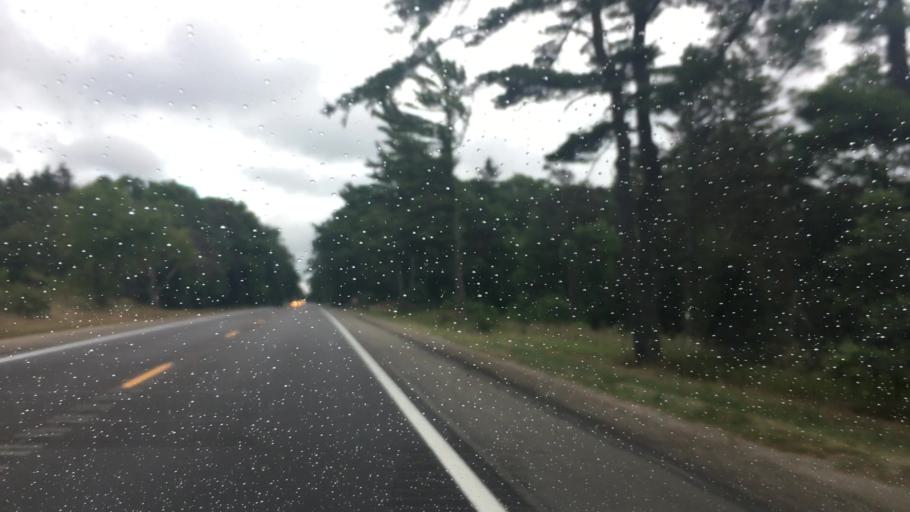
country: US
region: Michigan
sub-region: Ottawa County
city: Spring Lake
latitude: 42.9722
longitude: -86.1684
